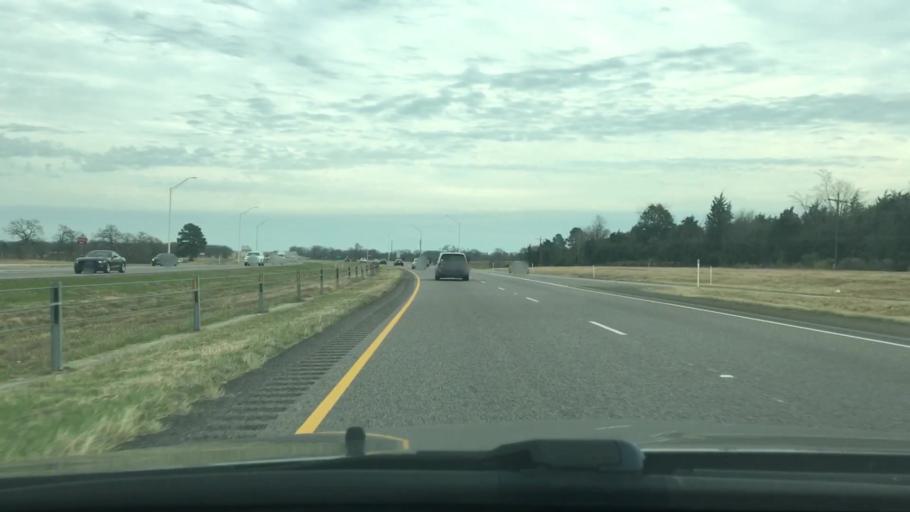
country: US
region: Texas
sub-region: Madison County
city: Madisonville
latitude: 30.9598
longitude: -95.8772
